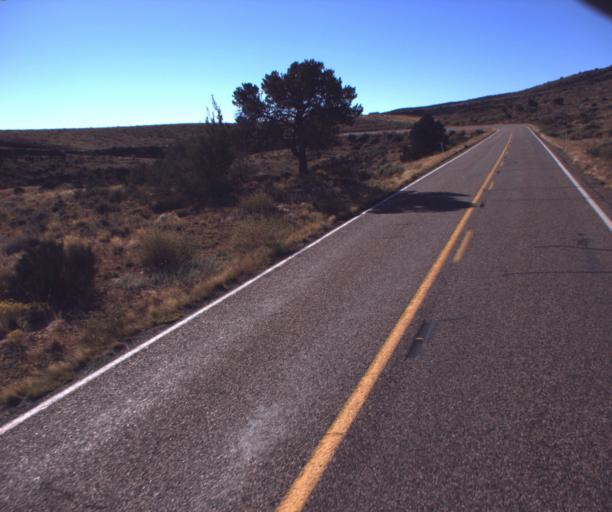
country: US
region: Arizona
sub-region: Coconino County
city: Fredonia
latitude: 36.7286
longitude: -112.0621
